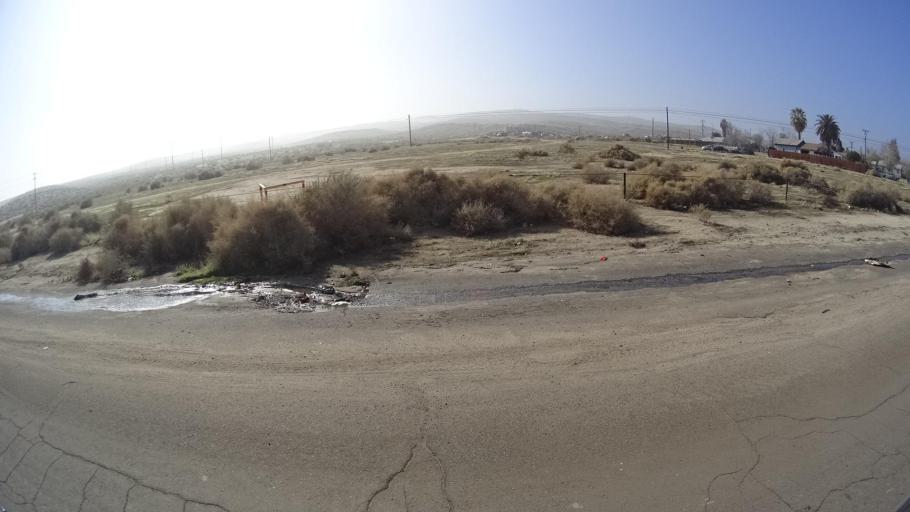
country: US
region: California
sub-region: Kern County
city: South Taft
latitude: 35.1324
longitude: -119.4482
